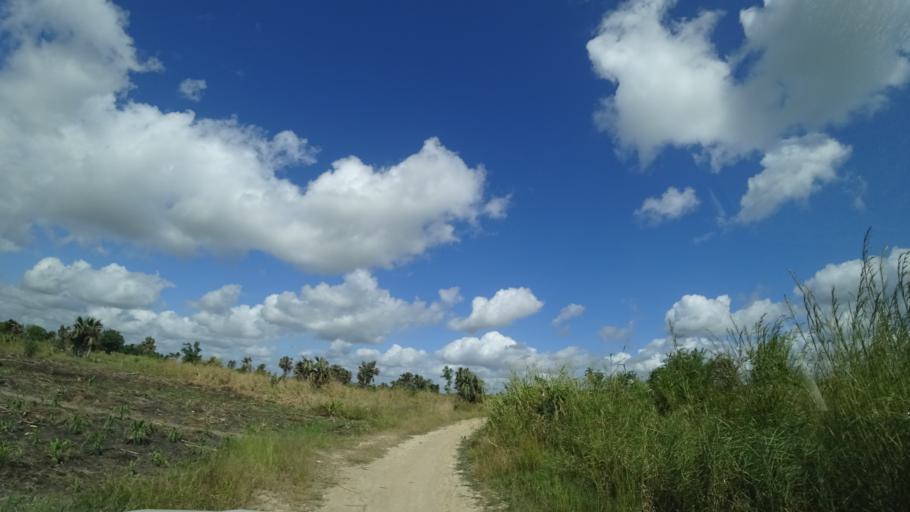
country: MZ
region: Sofala
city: Dondo
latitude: -19.3564
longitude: 34.5844
